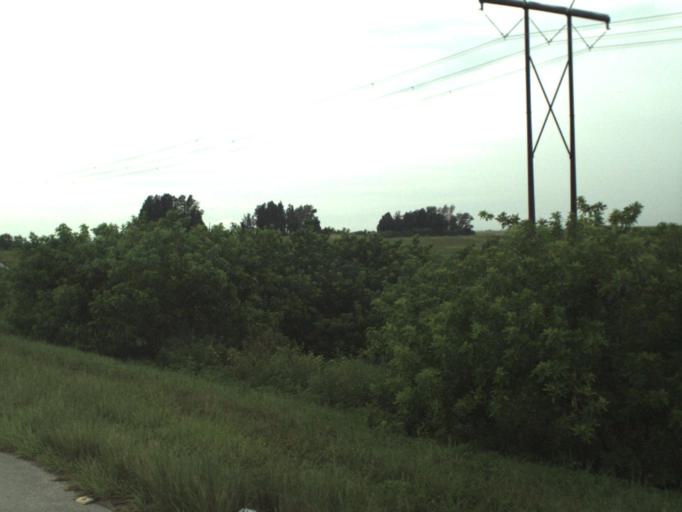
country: US
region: Florida
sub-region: Palm Beach County
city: Loxahatchee Groves
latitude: 26.6867
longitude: -80.3880
